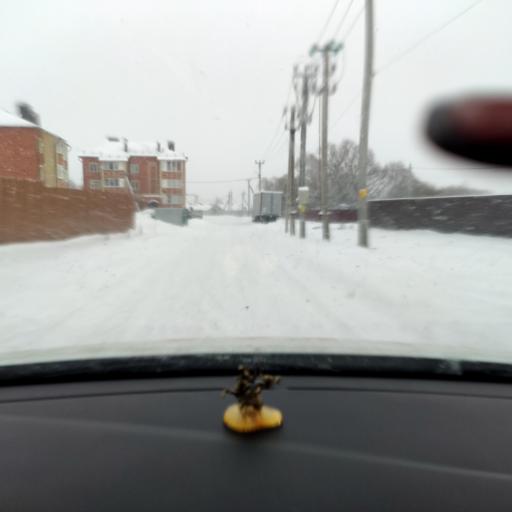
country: RU
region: Tatarstan
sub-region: Arskiy Rayon
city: Arsk
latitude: 56.0986
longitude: 49.8780
